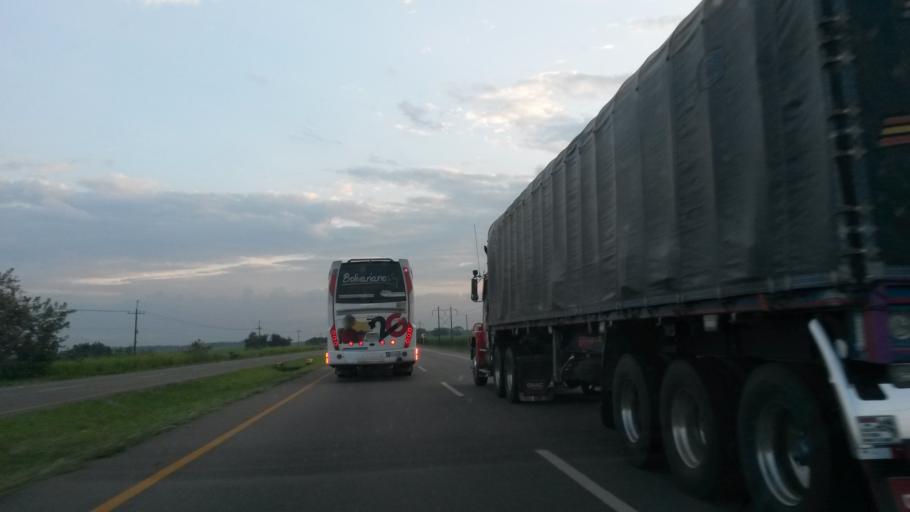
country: CO
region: Cauca
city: Caloto
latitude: 3.0981
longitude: -76.4694
